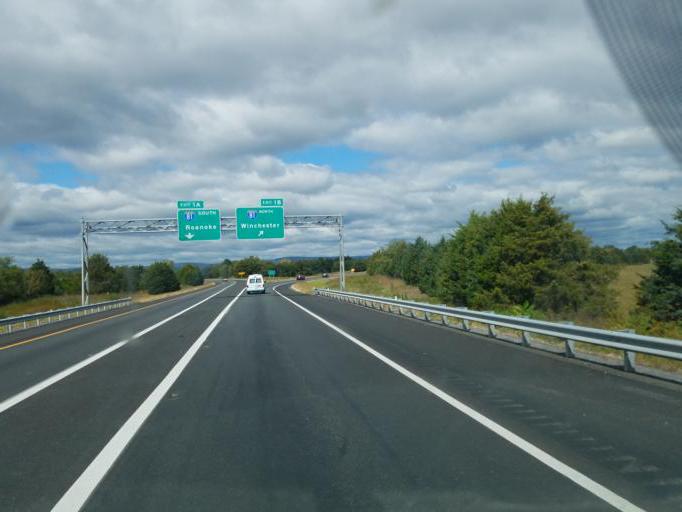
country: US
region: Virginia
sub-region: Frederick County
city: Middletown
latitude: 39.0074
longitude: -78.2928
